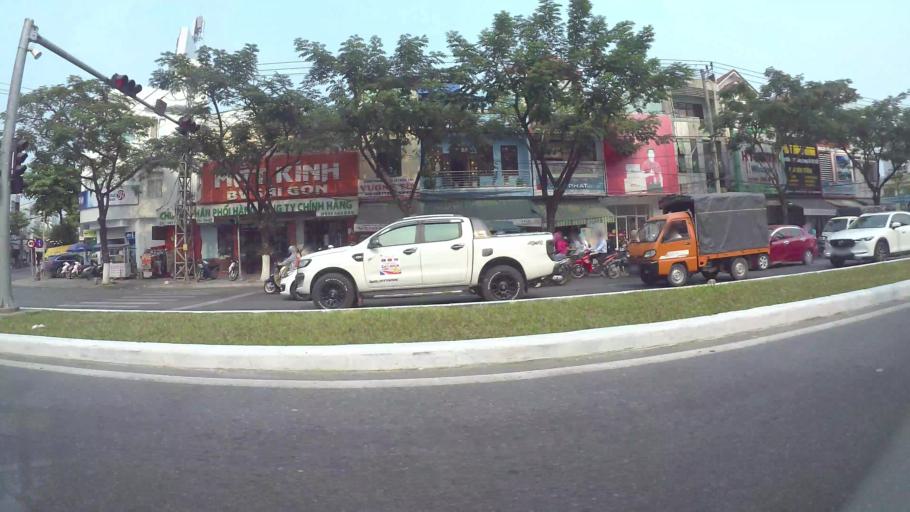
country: VN
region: Da Nang
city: Da Nang
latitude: 16.0453
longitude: 108.2098
